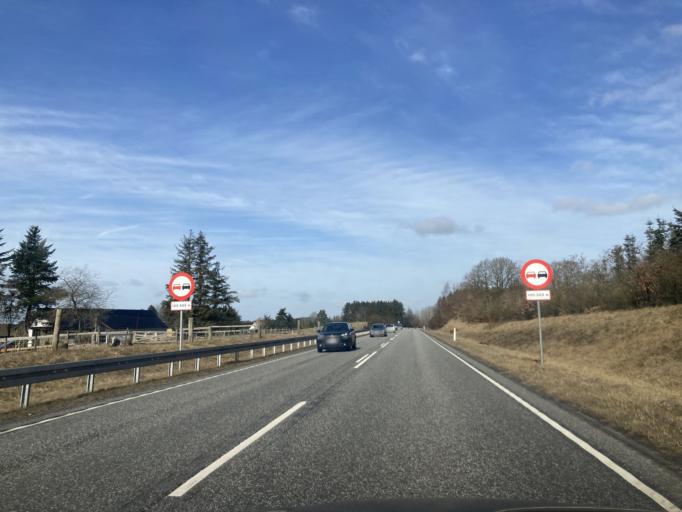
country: DK
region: Central Jutland
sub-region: Hedensted Kommune
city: Torring
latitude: 55.9735
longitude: 9.3980
